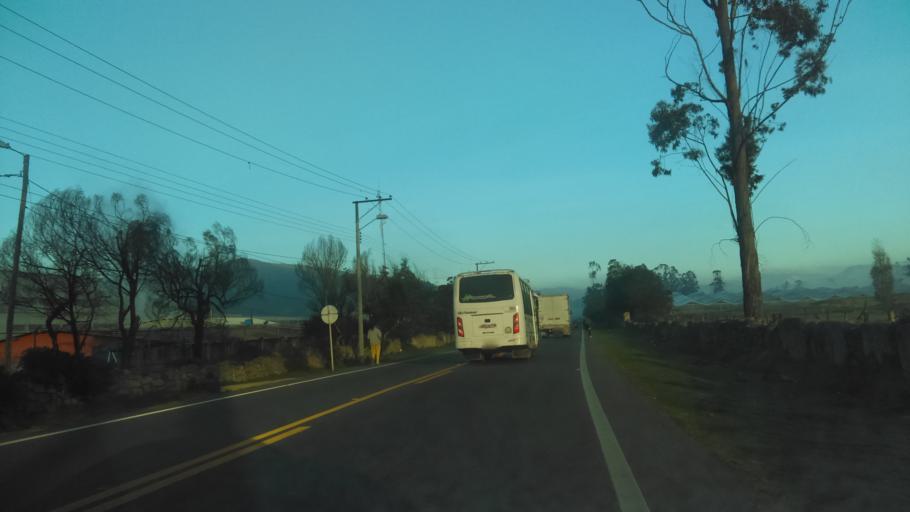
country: CO
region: Cundinamarca
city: Soacha
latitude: 4.5856
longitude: -74.2680
